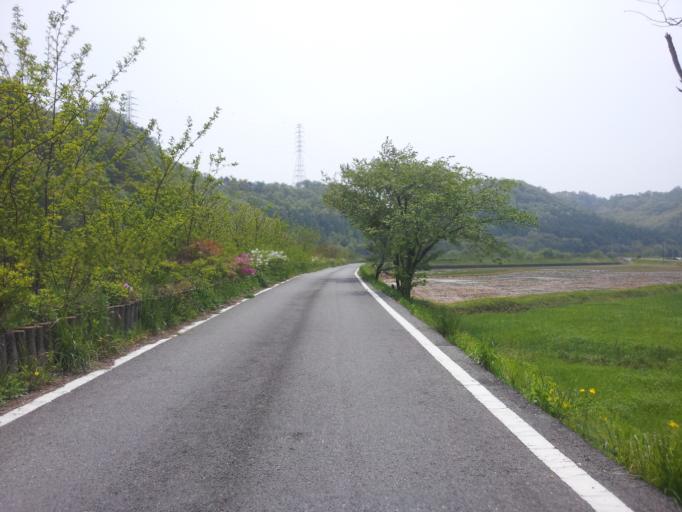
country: KR
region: Daejeon
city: Daejeon
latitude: 36.2596
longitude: 127.2940
